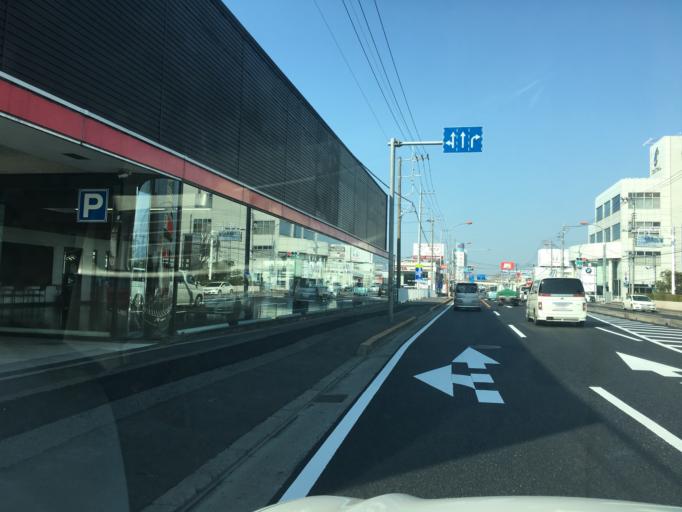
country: JP
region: Saitama
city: Kawagoe
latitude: 35.9118
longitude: 139.4982
